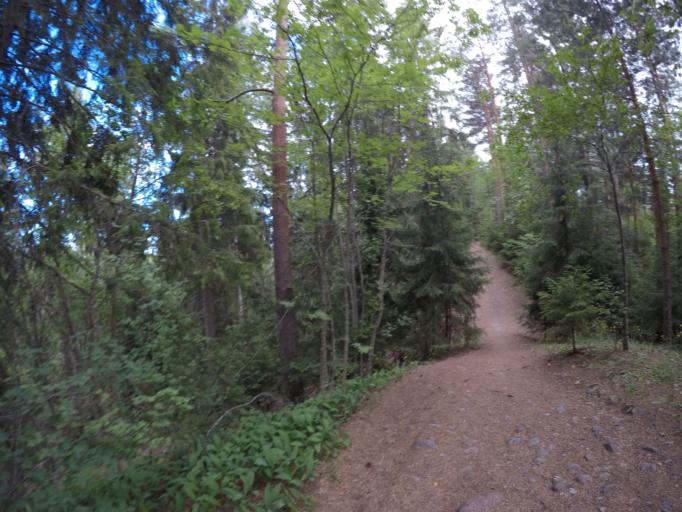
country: FI
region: Haeme
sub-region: Haemeenlinna
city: Parola
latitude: 61.0054
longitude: 24.4008
